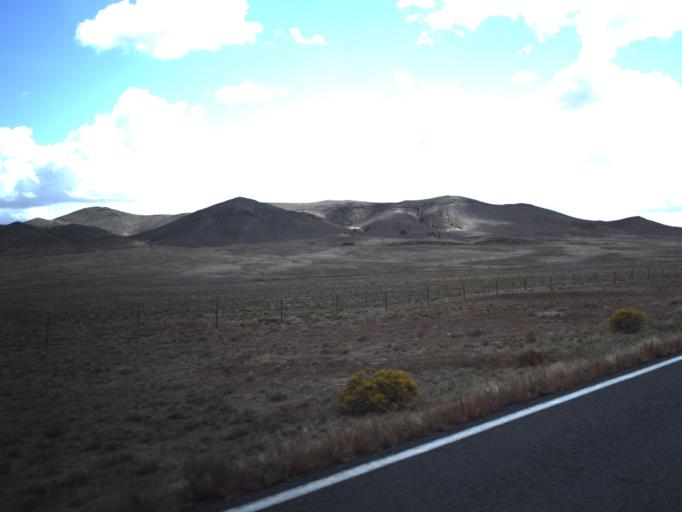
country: US
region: Utah
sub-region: Beaver County
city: Milford
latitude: 38.6477
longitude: -113.8670
